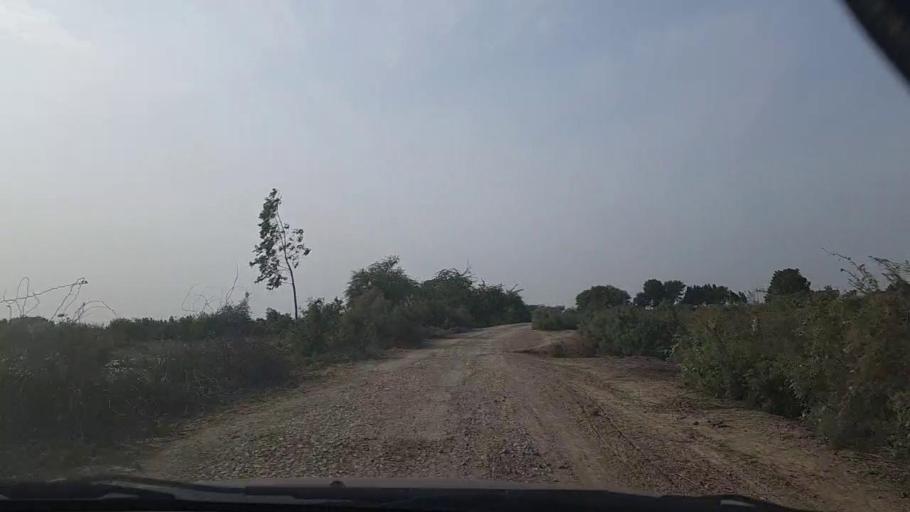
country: PK
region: Sindh
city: Thatta
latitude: 24.6138
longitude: 67.9483
